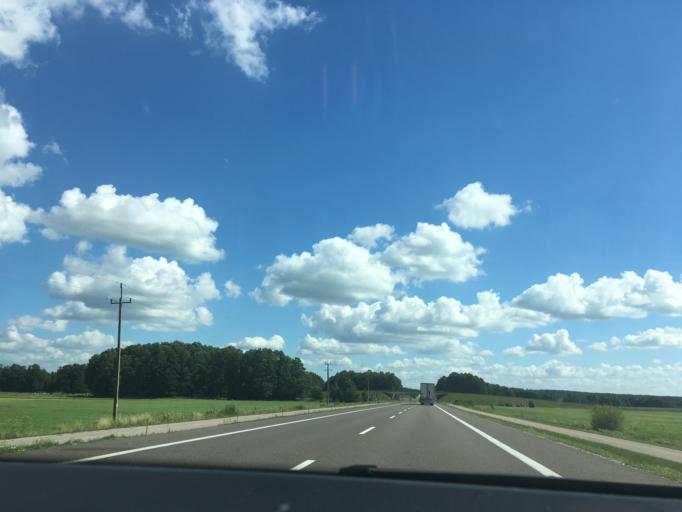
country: PL
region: Podlasie
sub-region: Powiat augustowski
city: Augustow
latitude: 53.7543
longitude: 23.0881
